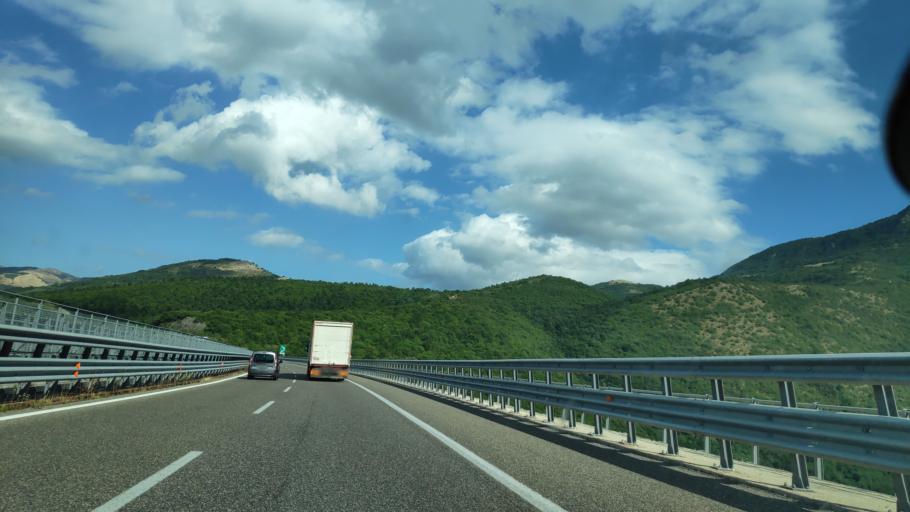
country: IT
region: Campania
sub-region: Provincia di Salerno
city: Pertosa
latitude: 40.5303
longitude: 15.4295
